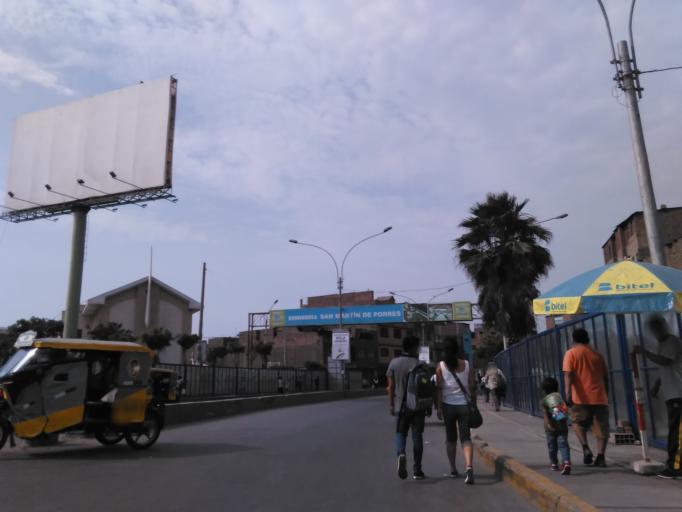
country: PE
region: Callao
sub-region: Callao
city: Callao
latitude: -12.0347
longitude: -77.0782
